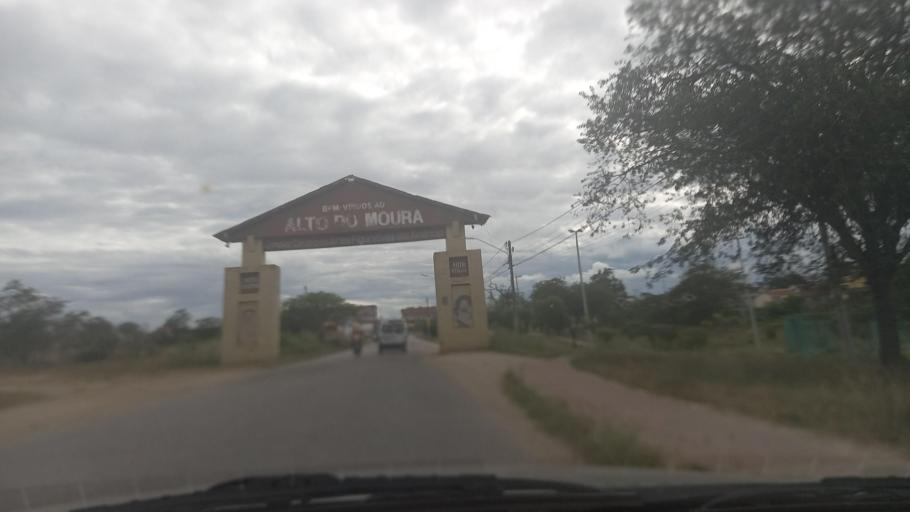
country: BR
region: Pernambuco
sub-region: Caruaru
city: Caruaru
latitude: -8.2896
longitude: -36.0252
